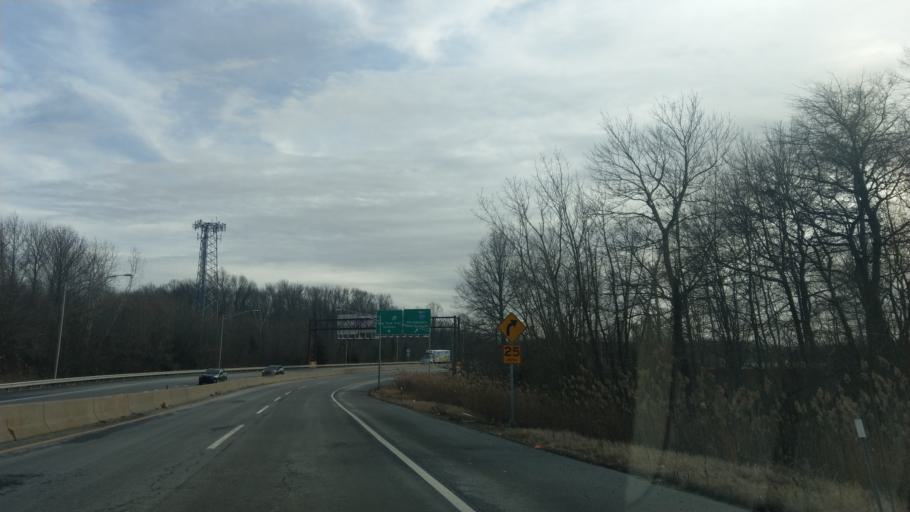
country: US
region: New Jersey
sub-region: Burlington County
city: Roebling
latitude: 40.1028
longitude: -74.7874
